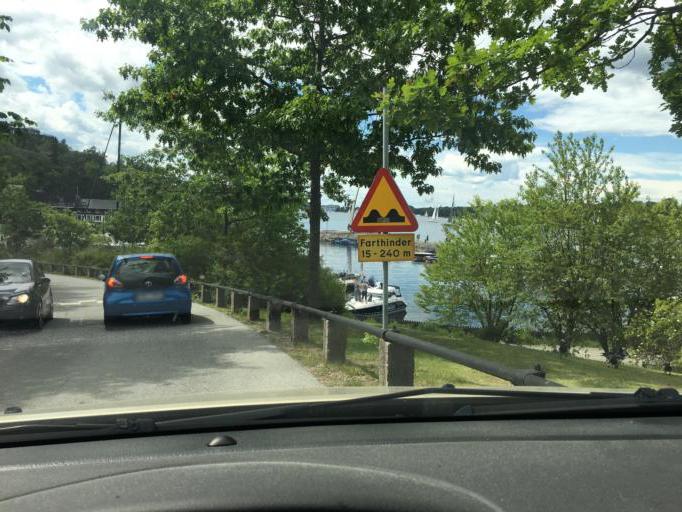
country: SE
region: Stockholm
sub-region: Nacka Kommun
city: Nacka
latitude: 59.3185
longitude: 18.1629
